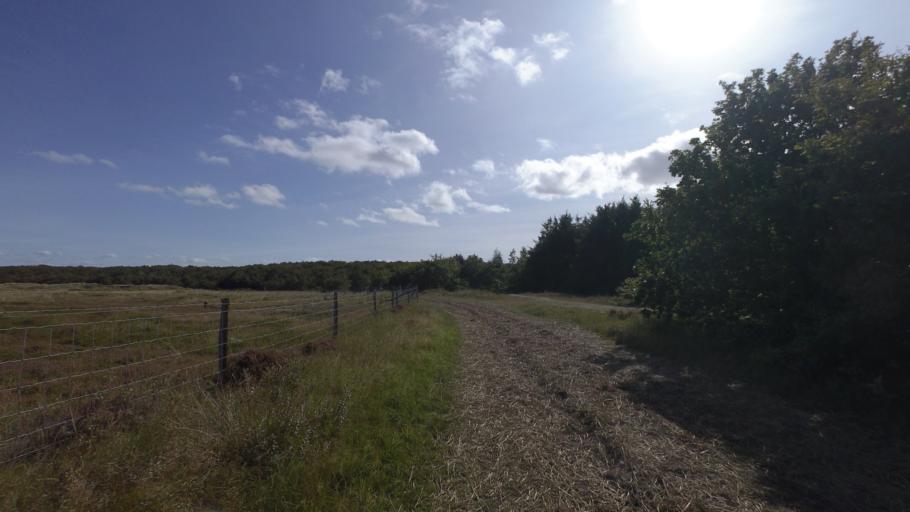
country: NL
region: Friesland
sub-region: Gemeente Ameland
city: Hollum
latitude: 53.4516
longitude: 5.6966
